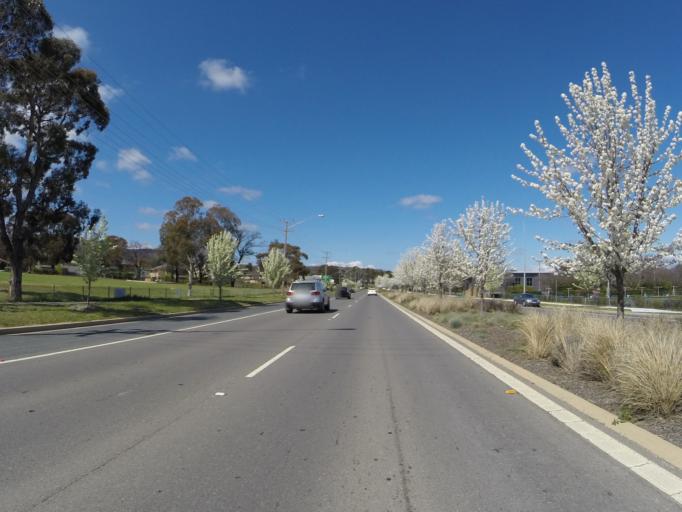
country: AU
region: New South Wales
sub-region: Queanbeyan
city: Queanbeyan
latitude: -35.3449
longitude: 149.2449
